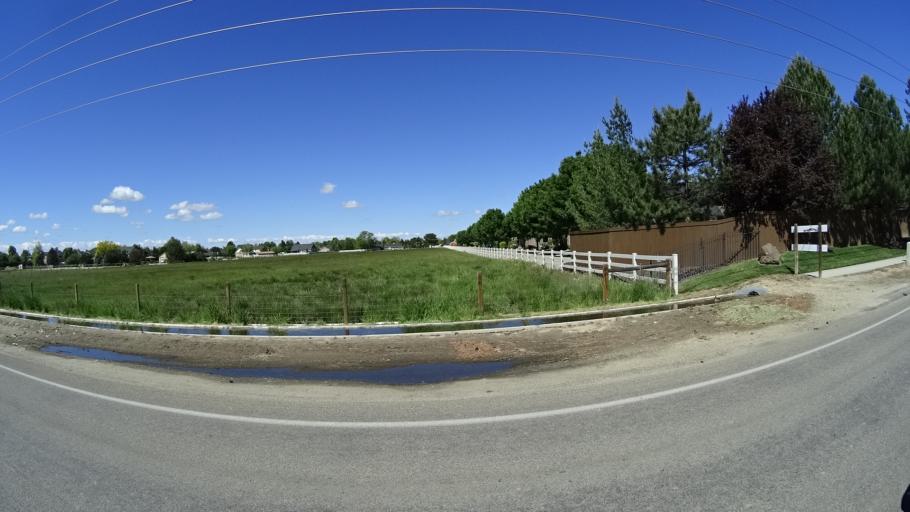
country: US
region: Idaho
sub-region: Ada County
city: Meridian
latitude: 43.6428
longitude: -116.3744
